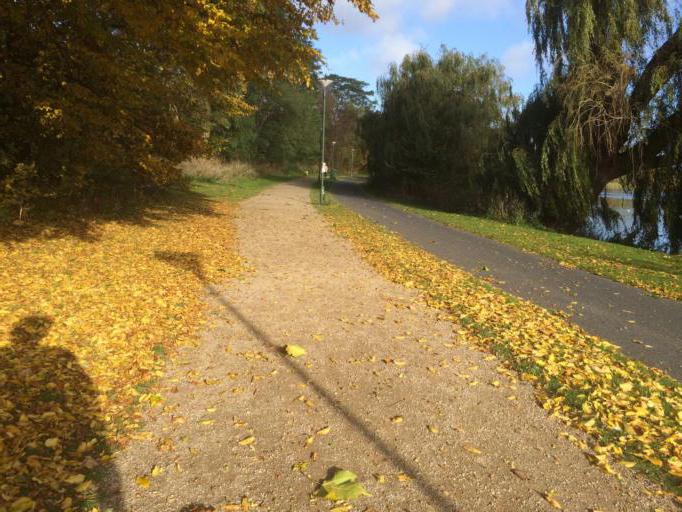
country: DK
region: Capital Region
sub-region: Kobenhavn
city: Vanlose
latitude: 55.7101
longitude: 12.4859
